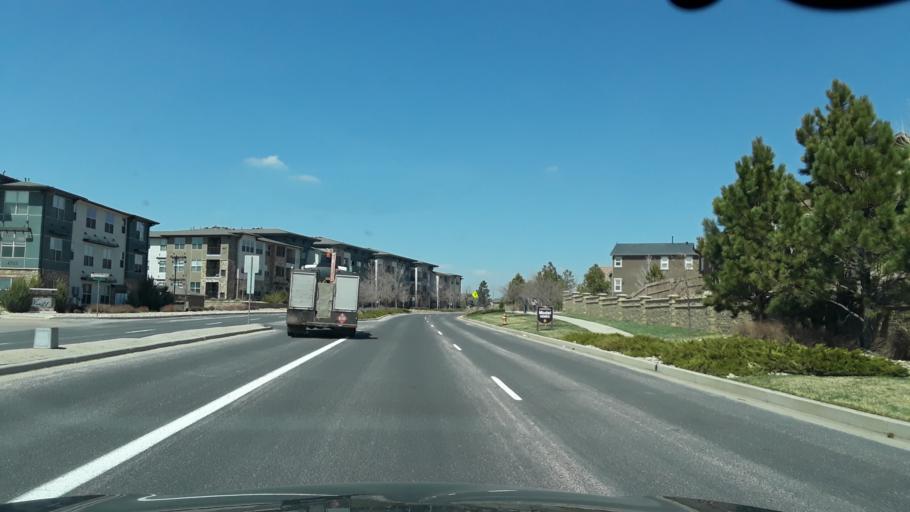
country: US
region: Colorado
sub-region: El Paso County
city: Black Forest
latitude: 38.9737
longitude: -104.7396
